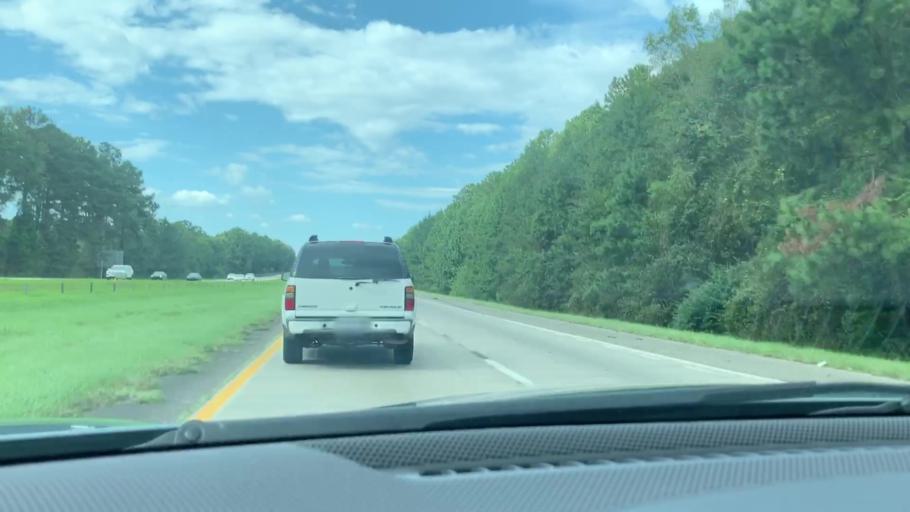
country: US
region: South Carolina
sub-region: Hampton County
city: Yemassee
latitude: 32.6381
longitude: -80.8822
